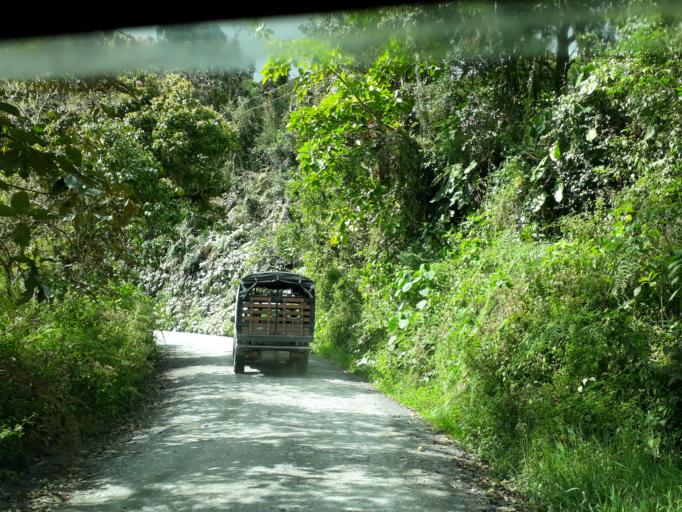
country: CO
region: Cundinamarca
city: Pacho
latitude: 5.2580
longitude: -74.1880
